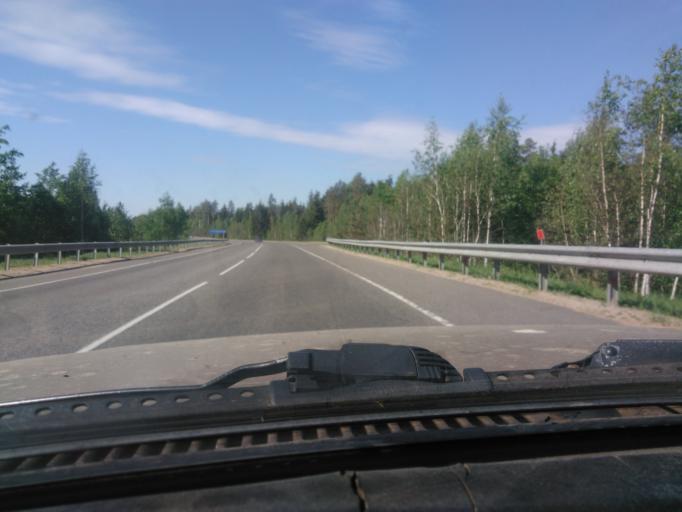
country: BY
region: Mogilev
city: Myazhysyatki
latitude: 53.8068
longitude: 30.2108
